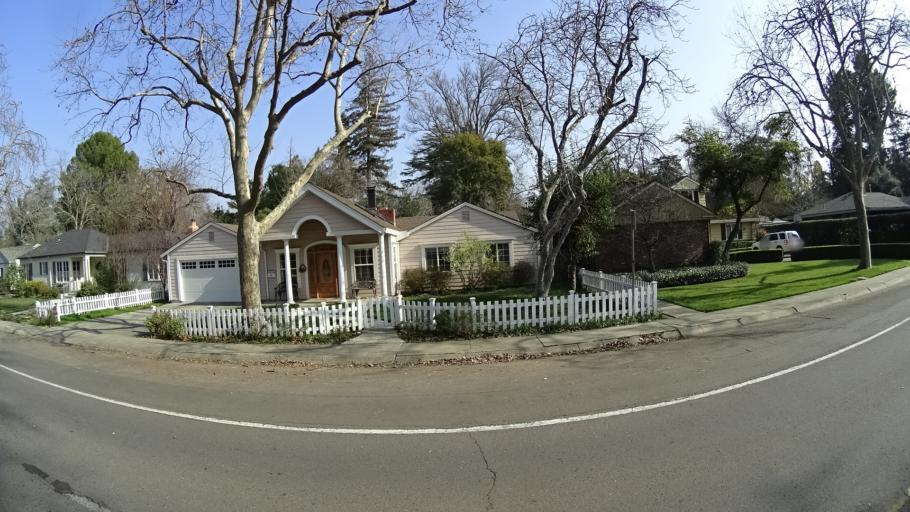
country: US
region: California
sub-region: Yolo County
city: Davis
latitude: 38.5486
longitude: -121.7528
